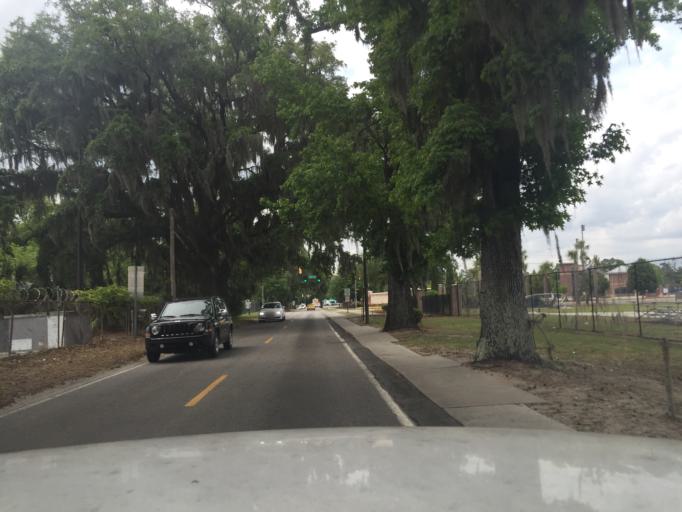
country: US
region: Georgia
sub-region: Chatham County
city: Thunderbolt
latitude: 32.0249
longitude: -81.0696
